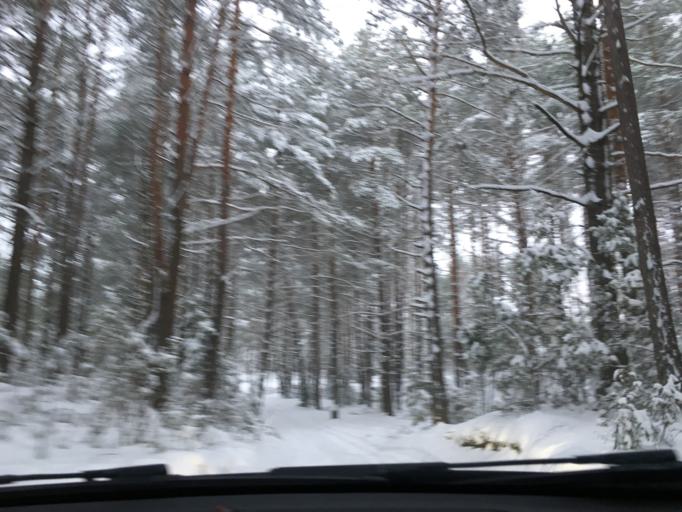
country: LT
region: Alytaus apskritis
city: Druskininkai
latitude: 53.9218
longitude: 24.1907
